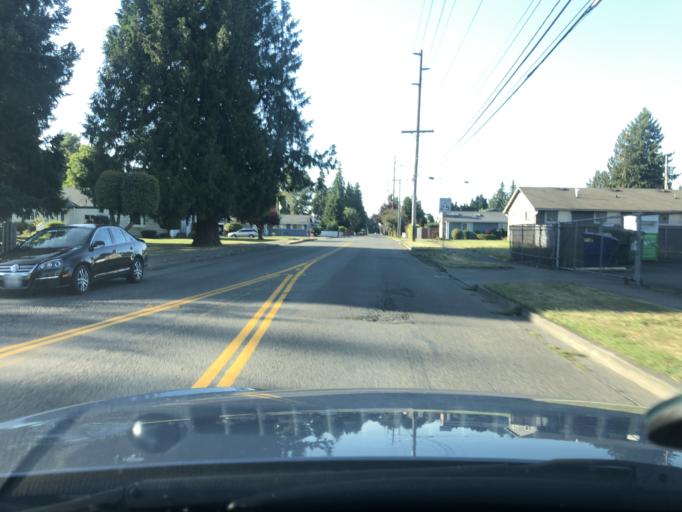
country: US
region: Washington
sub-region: King County
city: Auburn
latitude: 47.2834
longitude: -122.2134
